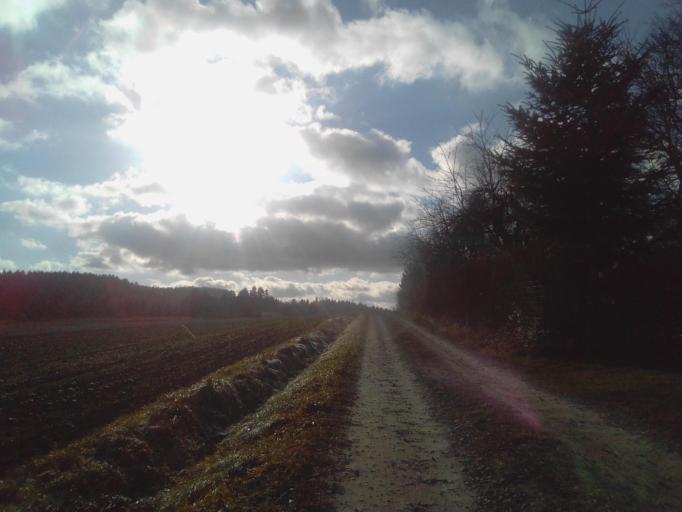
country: PL
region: Subcarpathian Voivodeship
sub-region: Powiat strzyzowski
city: Polomia
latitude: 49.8991
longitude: 21.8569
